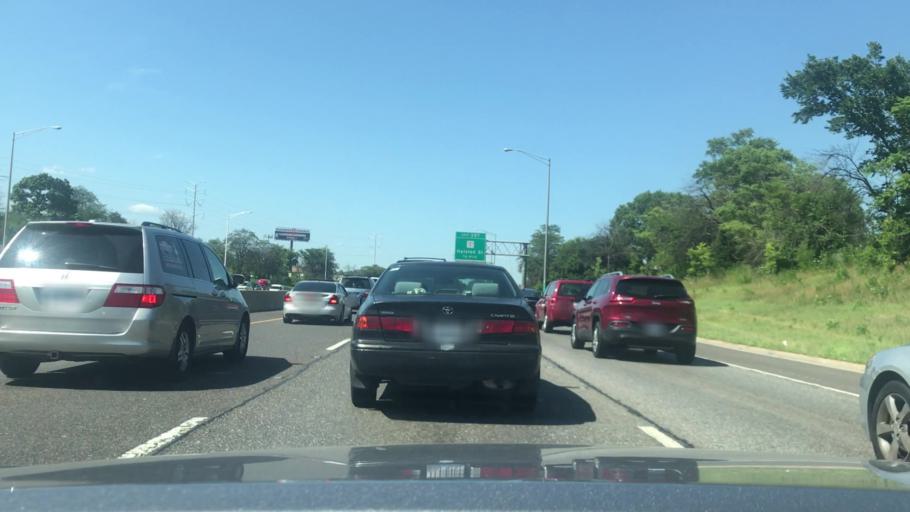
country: US
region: Illinois
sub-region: Cook County
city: Calumet Park
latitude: 41.7088
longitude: -87.6530
